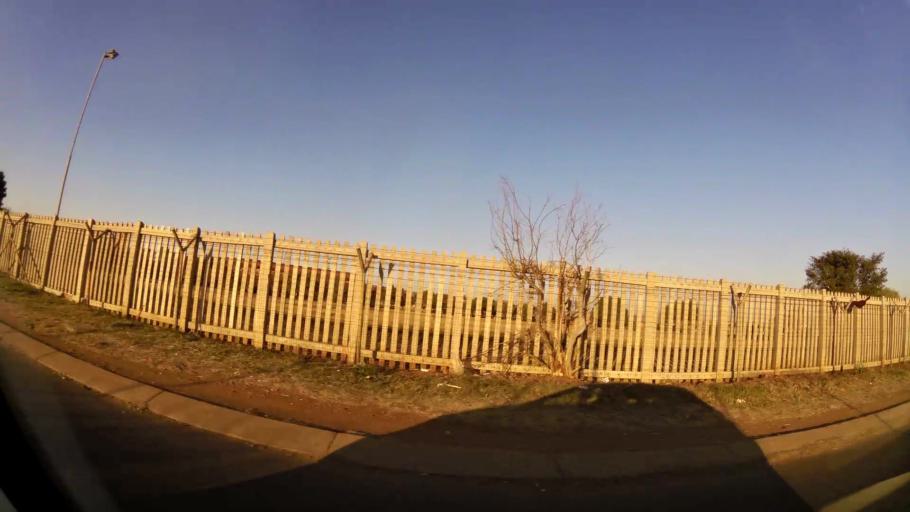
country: ZA
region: Gauteng
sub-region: City of Tshwane Metropolitan Municipality
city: Cullinan
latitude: -25.7224
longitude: 28.3972
